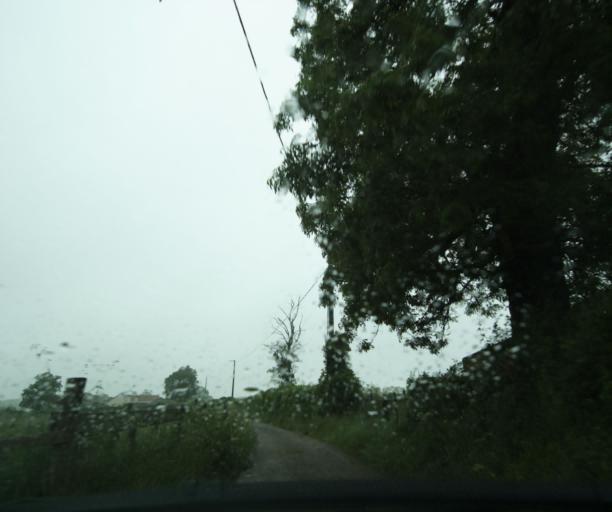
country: FR
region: Bourgogne
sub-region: Departement de Saone-et-Loire
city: La Clayette
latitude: 46.3678
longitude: 4.3527
